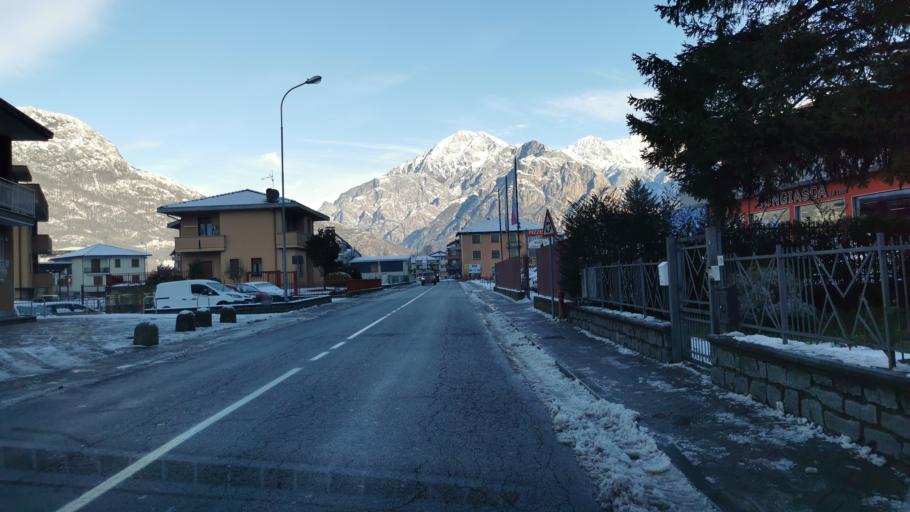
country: IT
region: Lombardy
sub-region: Provincia di Sondrio
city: Dubino
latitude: 46.1695
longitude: 9.4324
